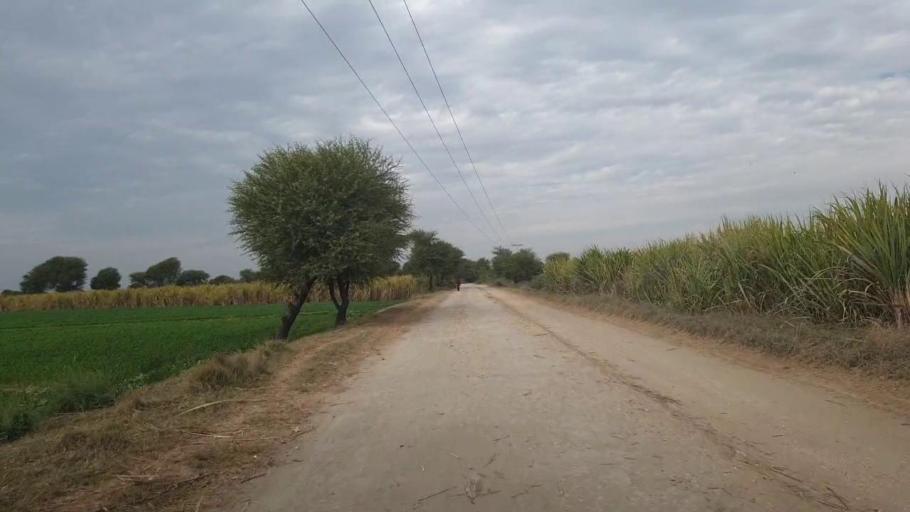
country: PK
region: Sindh
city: Jhol
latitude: 26.0200
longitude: 68.8750
